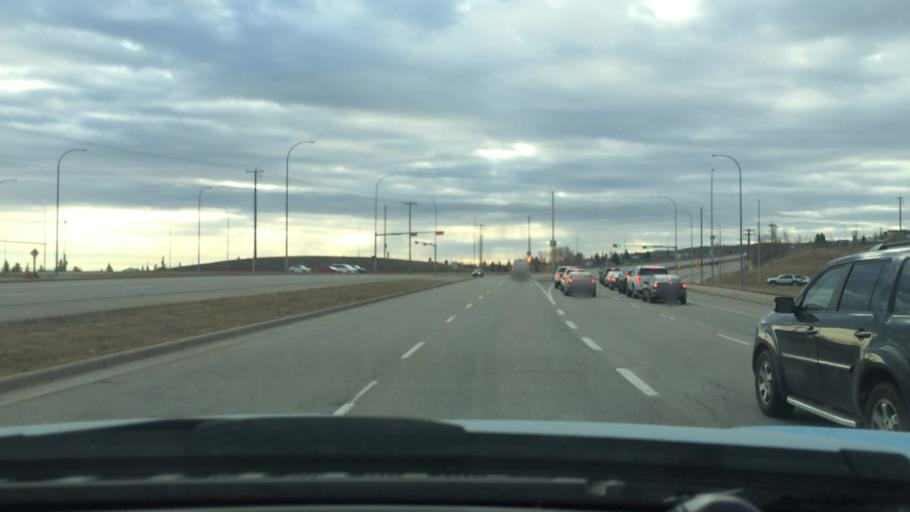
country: CA
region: Alberta
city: Calgary
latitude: 51.1436
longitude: -114.1250
